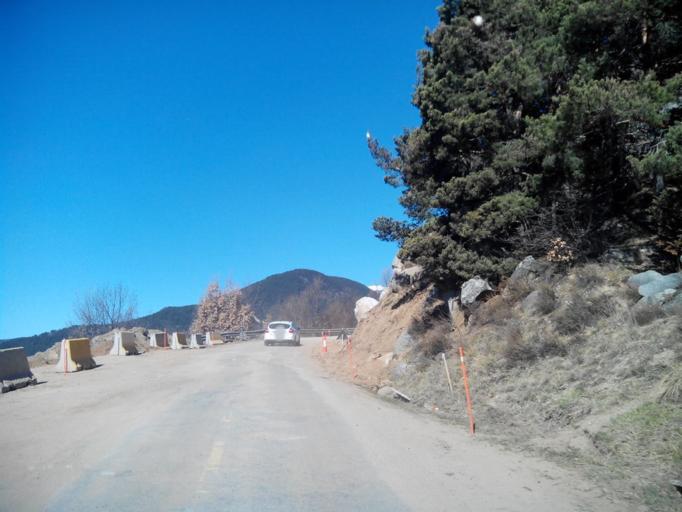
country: ES
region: Catalonia
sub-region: Provincia de Lleida
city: Lles de Cerdanya
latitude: 42.3847
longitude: 1.6869
